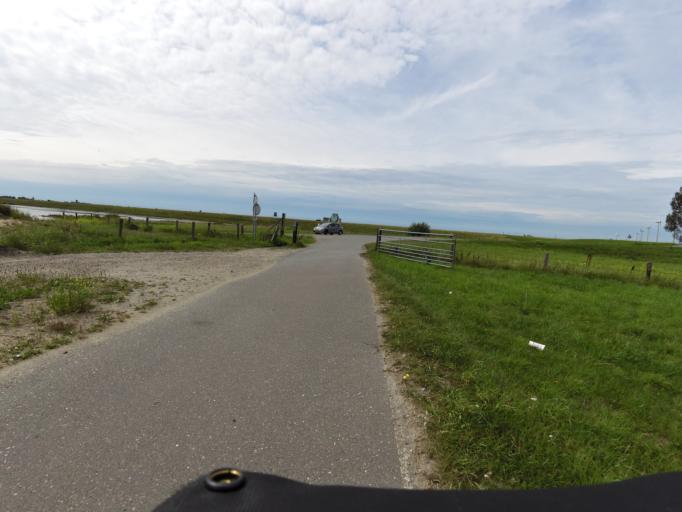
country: NL
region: South Holland
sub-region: Gemeente Goeree-Overflakkee
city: Middelharnis
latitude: 51.6862
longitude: 4.1661
